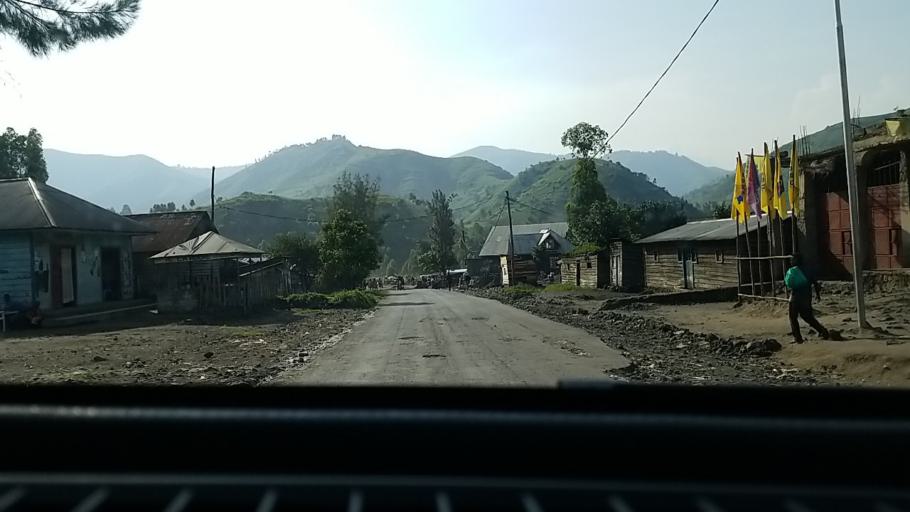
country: CD
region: Nord Kivu
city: Sake
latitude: -1.5710
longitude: 29.0495
